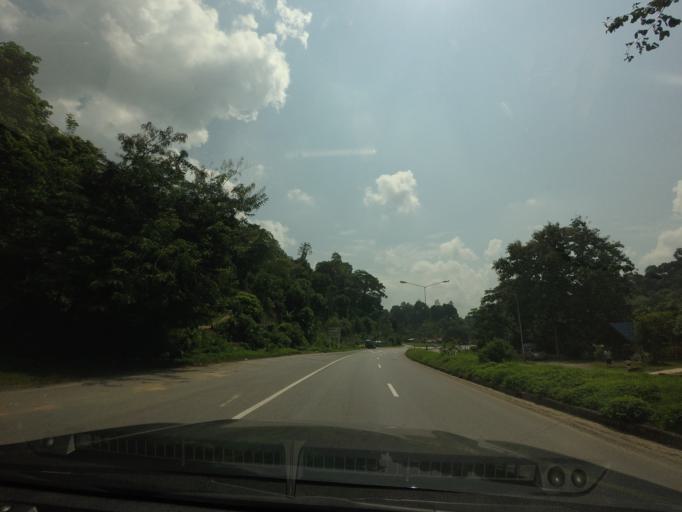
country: TH
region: Uttaradit
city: Lap Lae
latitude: 17.8101
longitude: 100.1081
